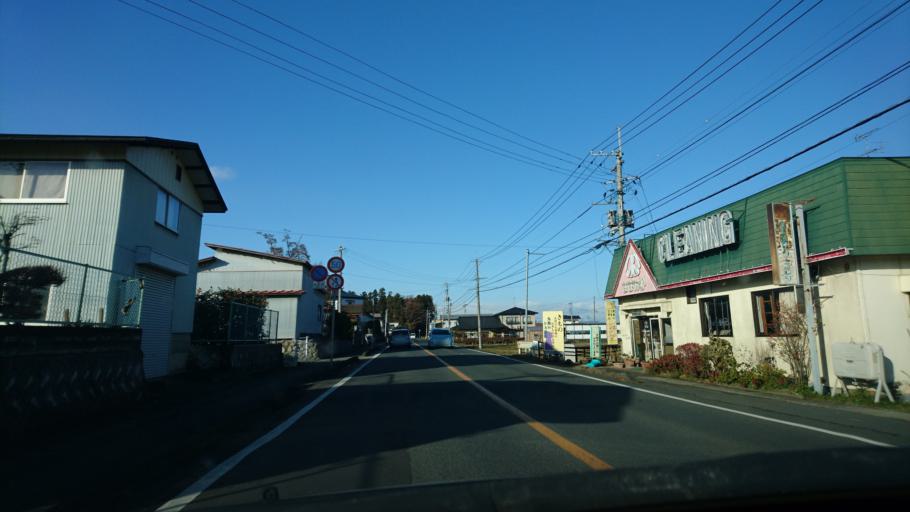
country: JP
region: Iwate
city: Mizusawa
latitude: 39.1186
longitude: 141.1652
